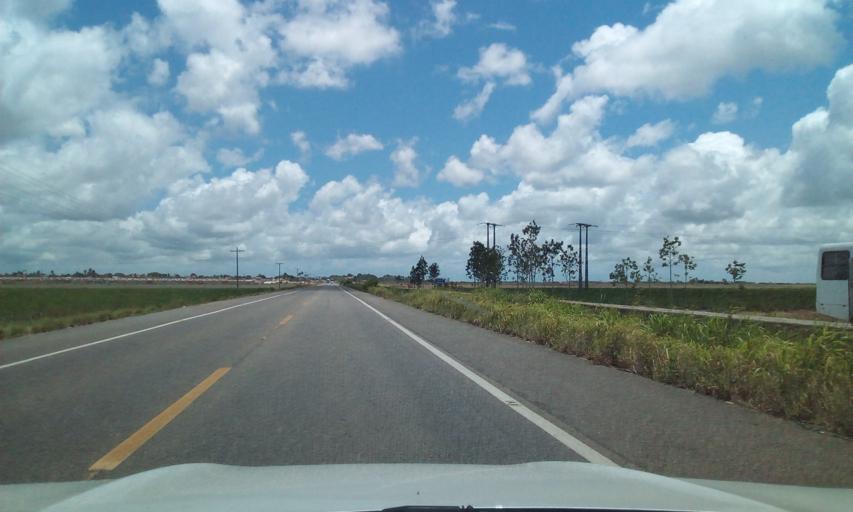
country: BR
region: Alagoas
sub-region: Campo Alegre
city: Campo Alegre
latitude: -9.9025
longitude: -36.2333
